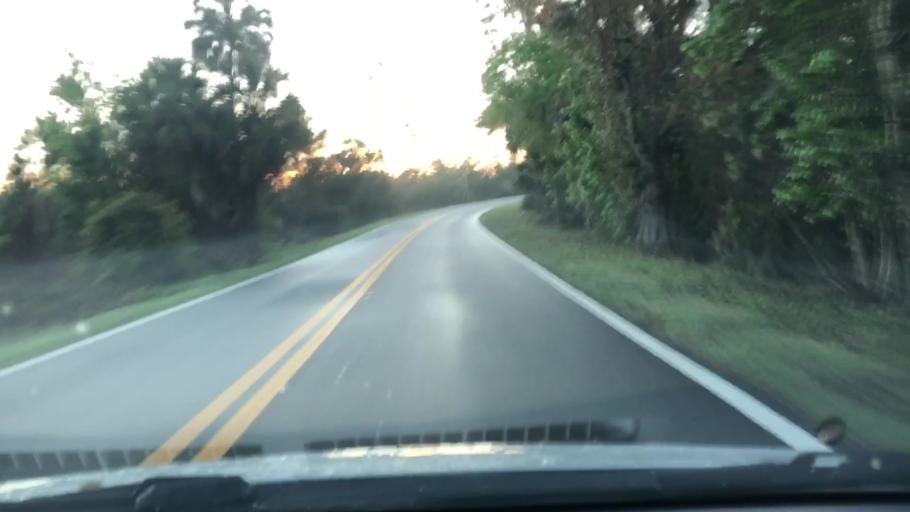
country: US
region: Florida
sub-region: Seminole County
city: Midway
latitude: 28.8474
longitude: -81.1751
